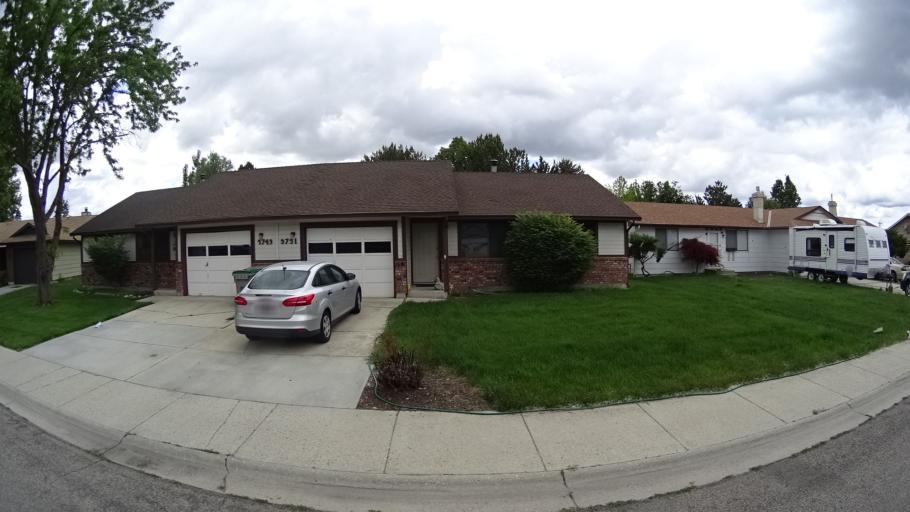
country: US
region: Idaho
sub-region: Ada County
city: Garden City
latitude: 43.6600
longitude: -116.2602
